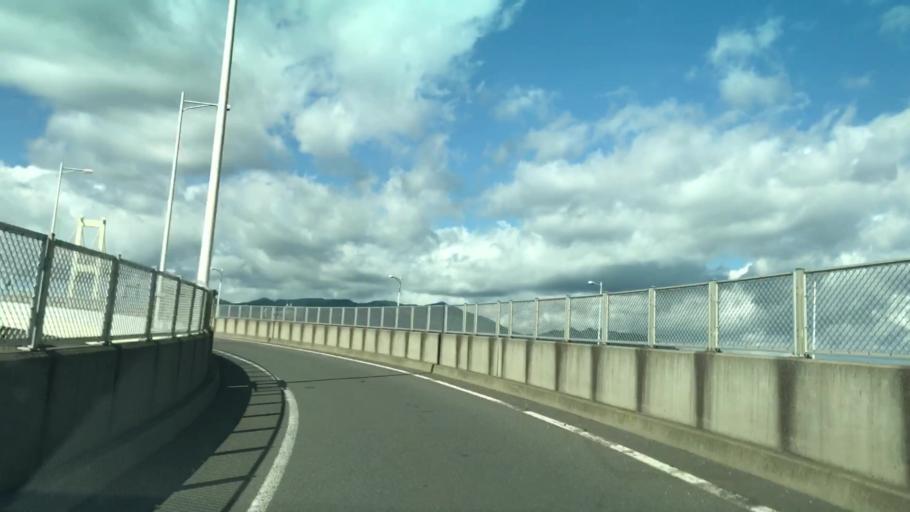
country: JP
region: Hokkaido
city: Muroran
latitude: 42.3423
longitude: 140.9493
